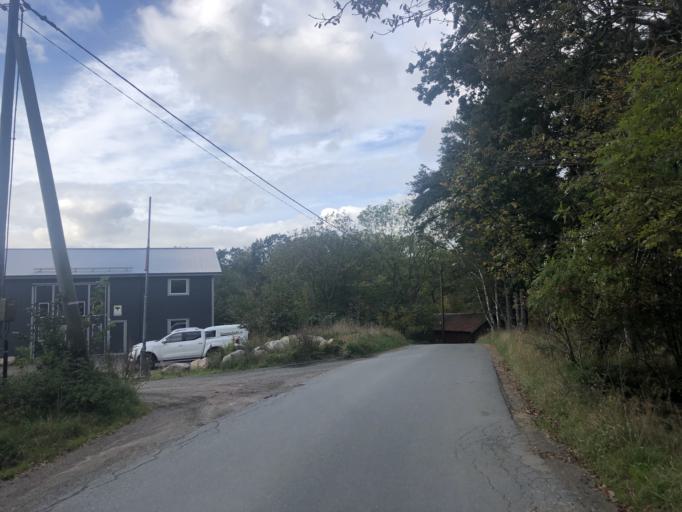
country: SE
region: Vaestra Goetaland
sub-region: Molndal
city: Moelndal
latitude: 57.6379
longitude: 11.9788
